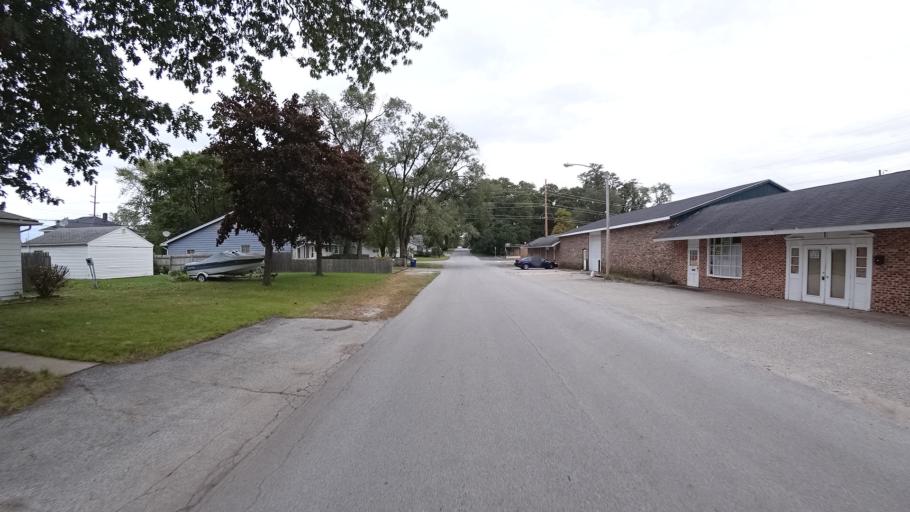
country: US
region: Indiana
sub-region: LaPorte County
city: Michigan City
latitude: 41.7017
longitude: -86.8914
